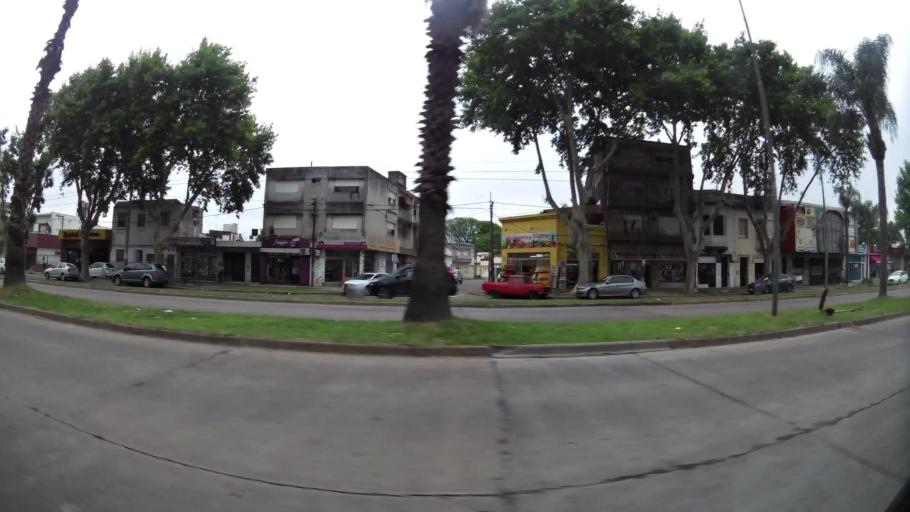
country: AR
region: Santa Fe
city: Granadero Baigorria
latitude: -32.9086
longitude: -60.6880
